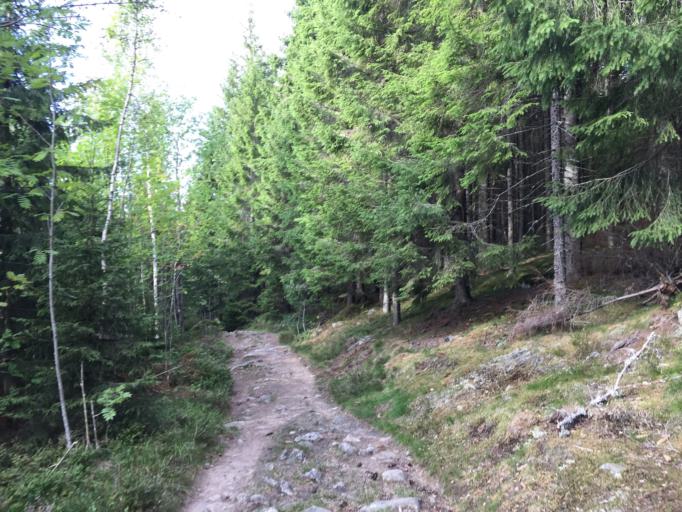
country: NO
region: Akershus
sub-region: Raelingen
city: Fjerdingby
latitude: 59.9148
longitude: 11.0288
